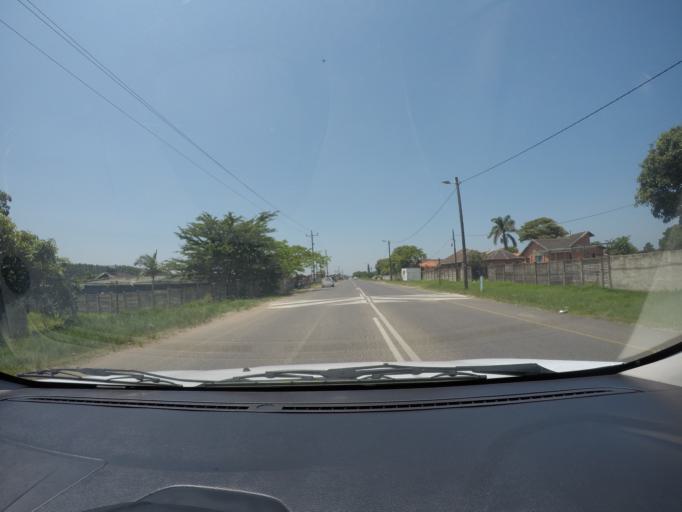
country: ZA
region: KwaZulu-Natal
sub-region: uThungulu District Municipality
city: eSikhawini
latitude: -28.8870
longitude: 31.8839
